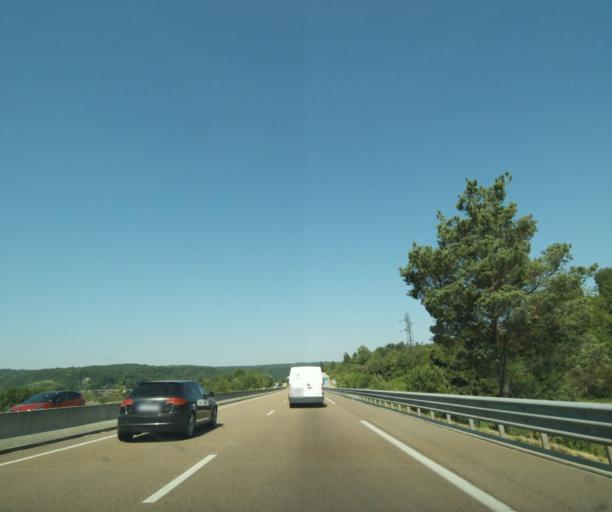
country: FR
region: Lorraine
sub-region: Departement de la Meuse
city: Ligny-en-Barrois
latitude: 48.6936
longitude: 5.3347
